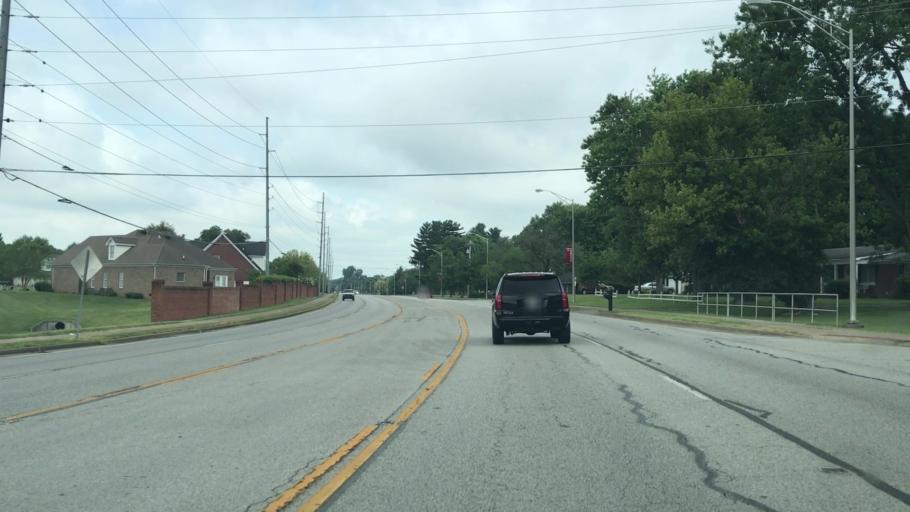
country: US
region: Kentucky
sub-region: Warren County
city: Bowling Green
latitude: 36.9882
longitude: -86.4053
